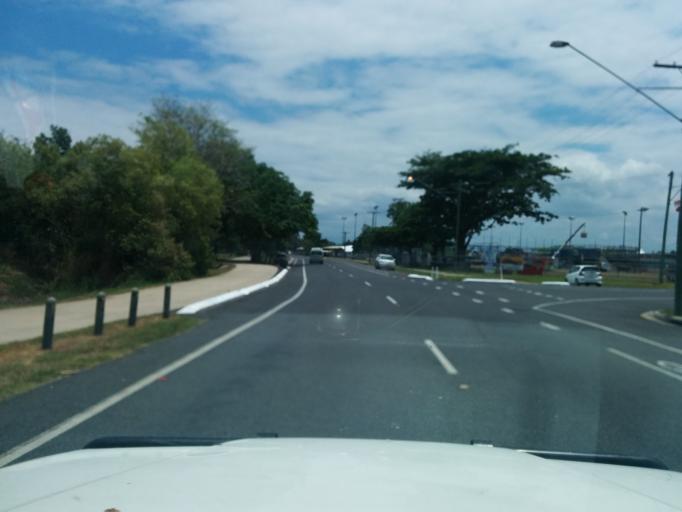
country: AU
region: Queensland
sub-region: Cairns
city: Cairns
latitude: -16.9000
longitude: 145.7586
